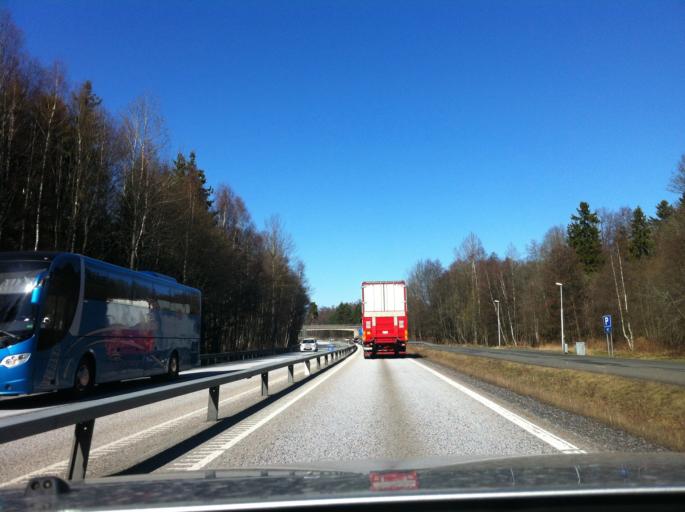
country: SE
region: Joenkoeping
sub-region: Jonkopings Kommun
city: Bankeryd
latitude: 57.8177
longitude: 14.1029
